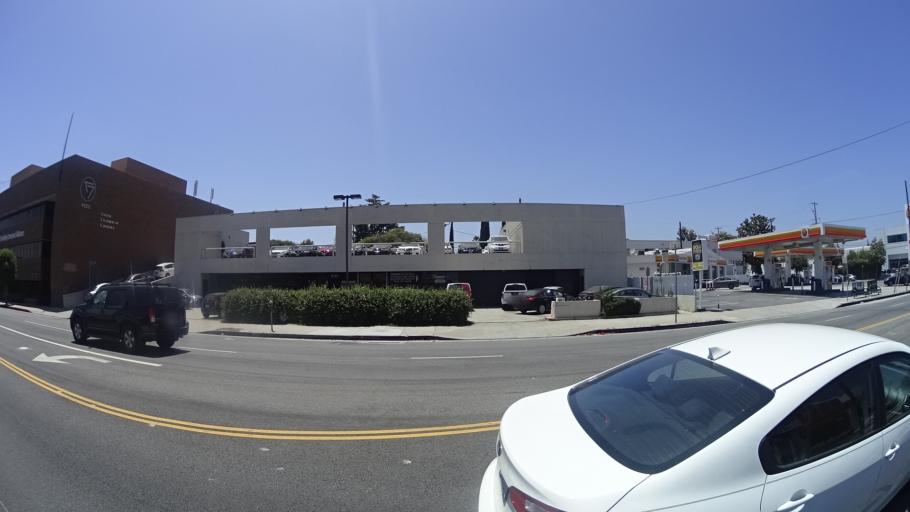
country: US
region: California
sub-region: Los Angeles County
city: Sherman Oaks
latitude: 34.1641
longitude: -118.4488
